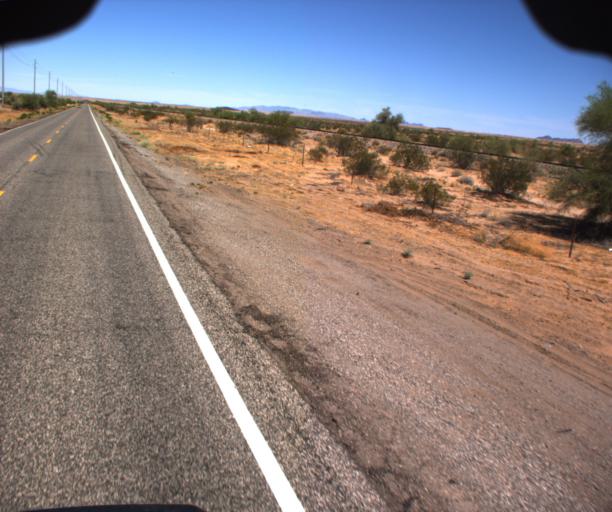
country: US
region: Arizona
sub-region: La Paz County
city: Cienega Springs
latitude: 33.9804
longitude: -114.0583
